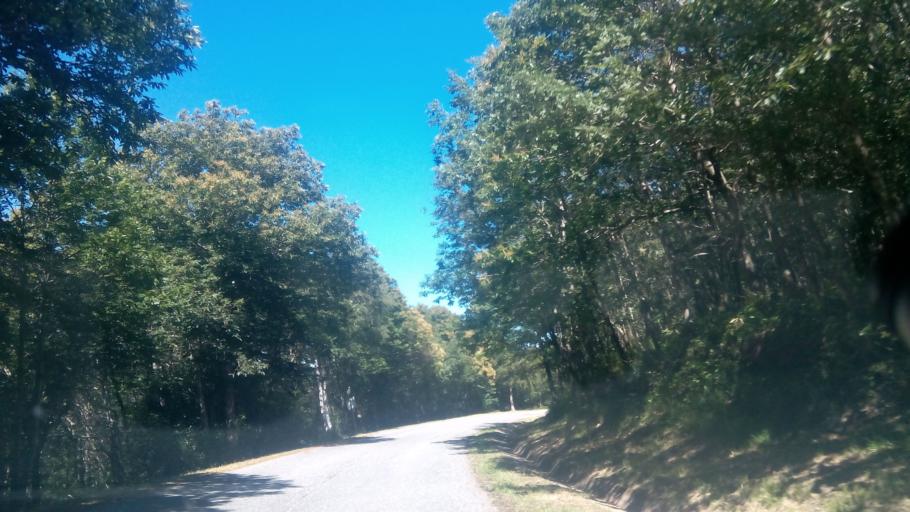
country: PT
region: Vila Real
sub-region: Mesao Frio
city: Mesao Frio
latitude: 41.2764
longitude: -7.8977
